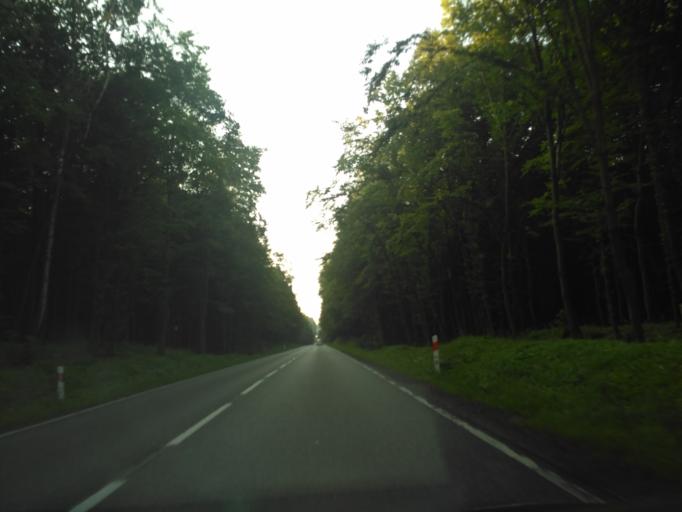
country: PL
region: Lublin Voivodeship
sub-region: Powiat krasnicki
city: Szastarka
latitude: 50.8589
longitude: 22.2815
